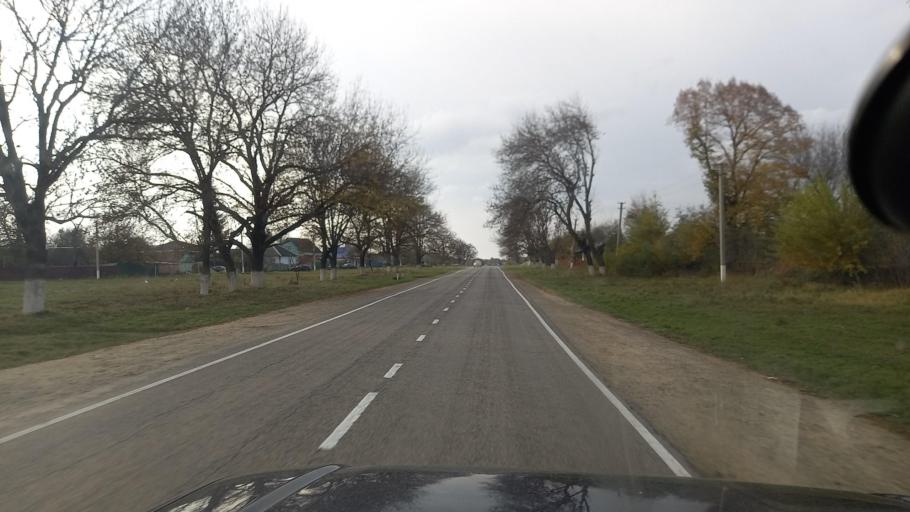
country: RU
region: Krasnodarskiy
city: Gubskaya
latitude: 44.3188
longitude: 40.6145
